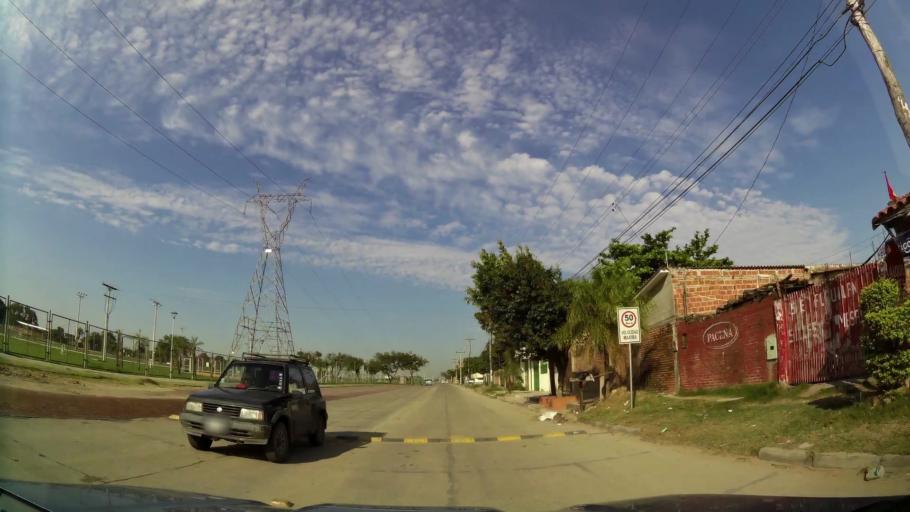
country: BO
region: Santa Cruz
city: Santa Cruz de la Sierra
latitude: -17.7329
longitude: -63.1402
